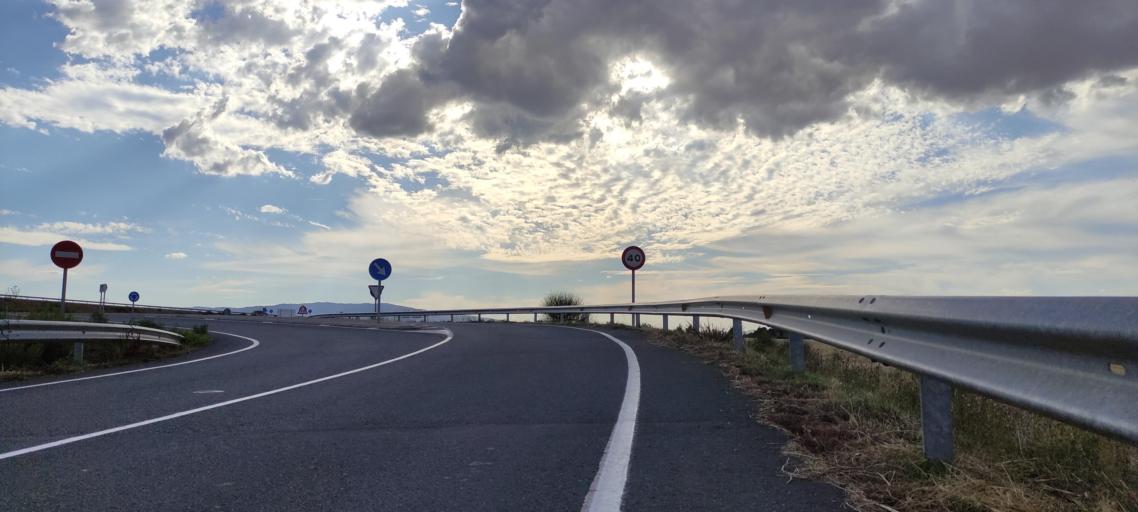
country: ES
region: La Rioja
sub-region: Provincia de La Rioja
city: Hervias
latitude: 42.4416
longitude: -2.8929
